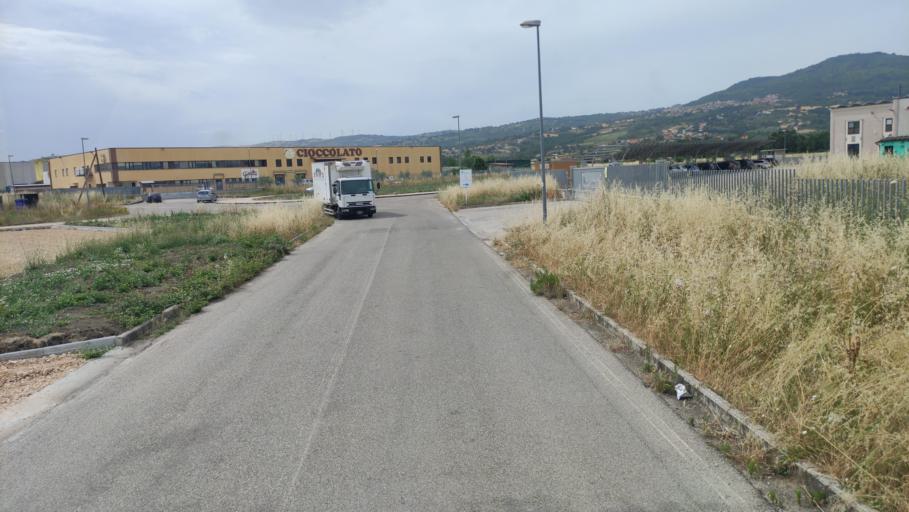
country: IT
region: Campania
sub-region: Provincia di Avellino
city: Sturno
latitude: 41.0496
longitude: 15.1219
